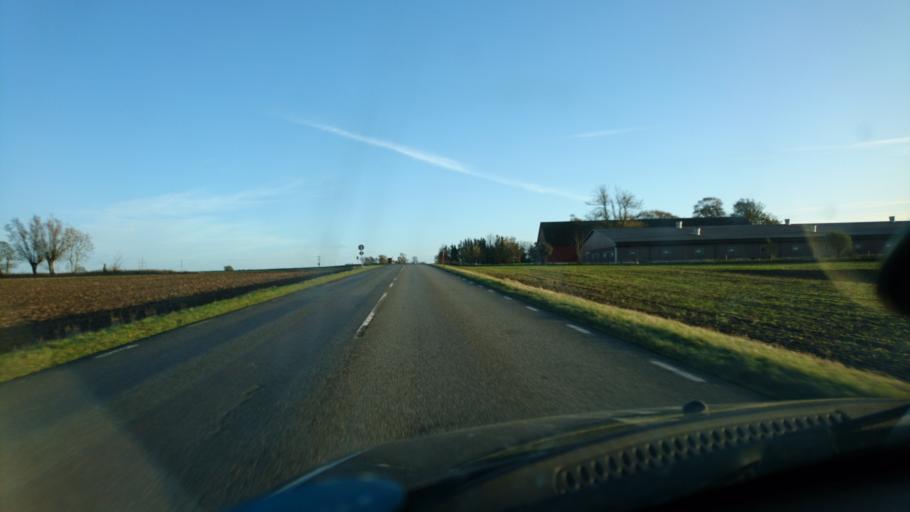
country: SE
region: Skane
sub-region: Simrishamns Kommun
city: Simrishamn
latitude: 55.4896
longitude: 14.1656
